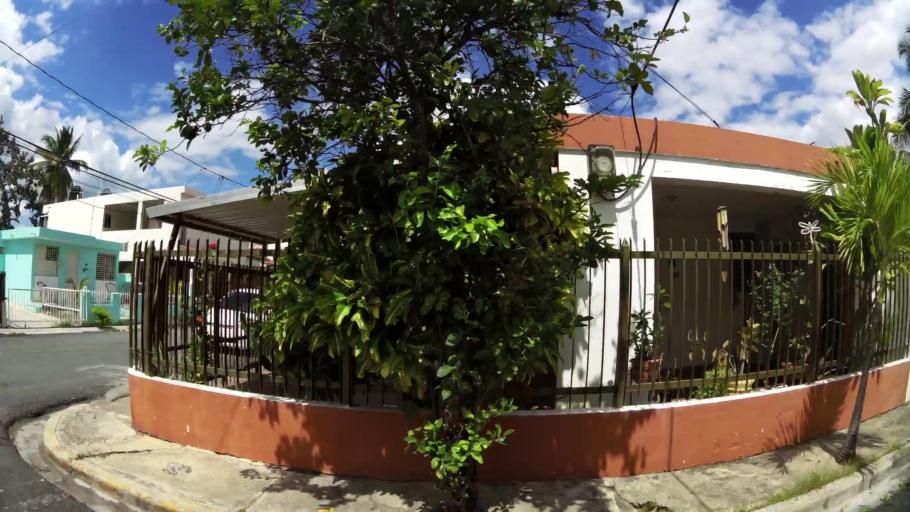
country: DO
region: Nacional
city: Ensanche Luperon
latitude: 18.5272
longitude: -69.8990
